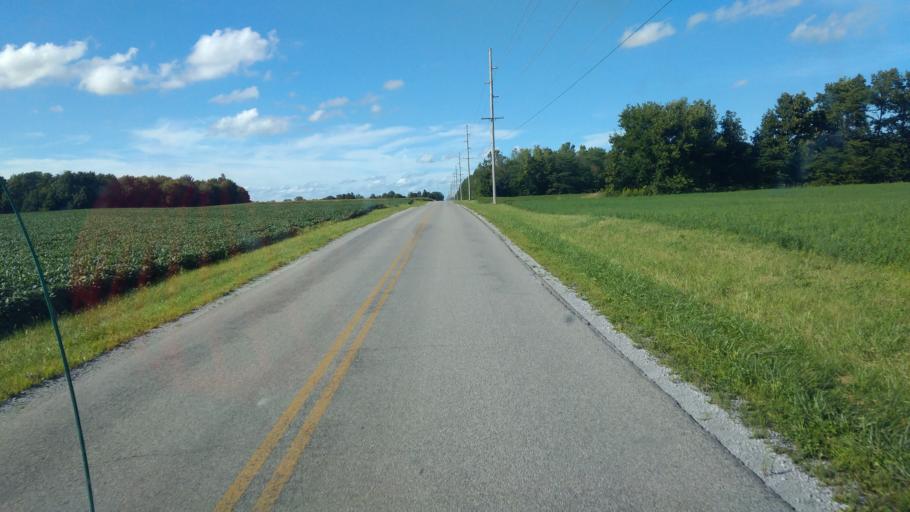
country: US
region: Ohio
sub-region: Hardin County
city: Kenton
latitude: 40.7071
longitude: -83.6535
